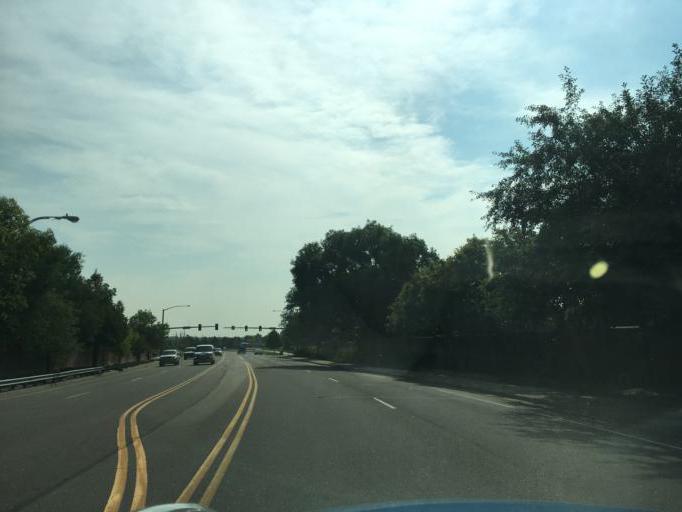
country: US
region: Colorado
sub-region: Adams County
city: Westminster
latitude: 39.8267
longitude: -105.0601
